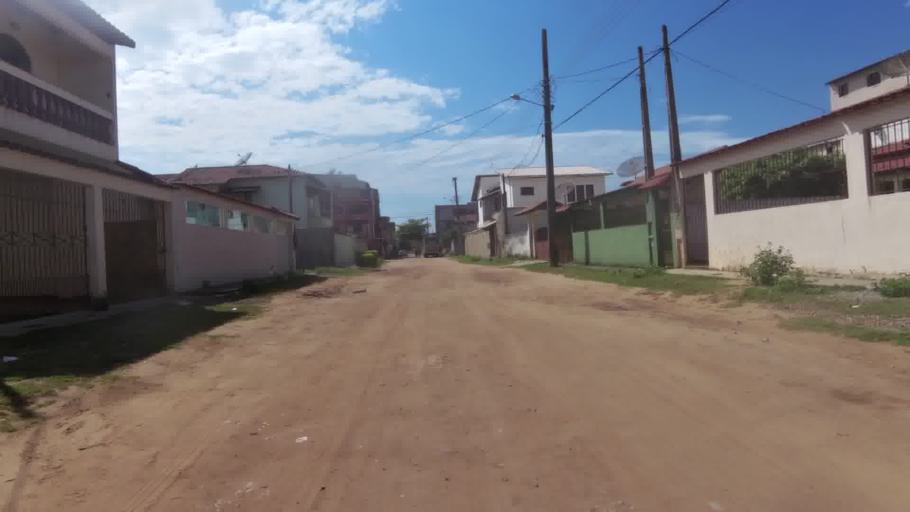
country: BR
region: Espirito Santo
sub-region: Piuma
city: Piuma
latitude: -20.8436
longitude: -40.7411
